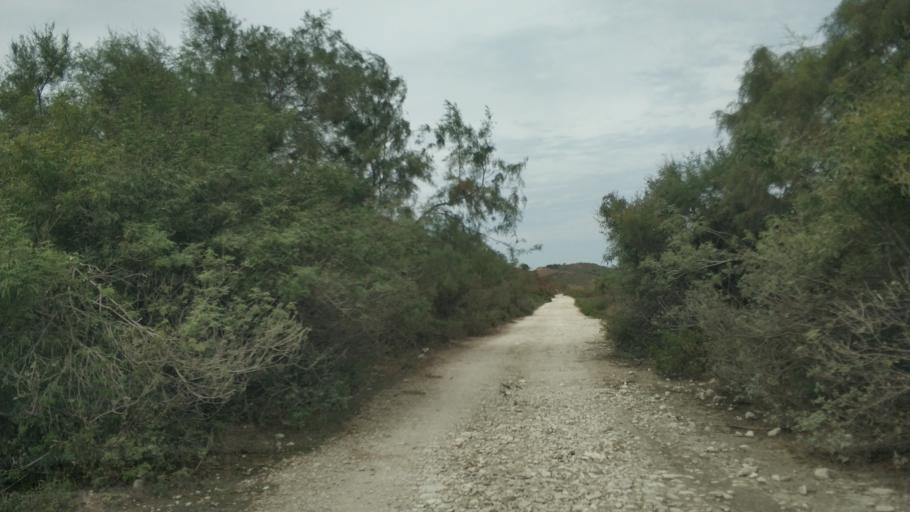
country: AL
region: Vlore
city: Vlore
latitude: 40.5120
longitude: 19.4002
